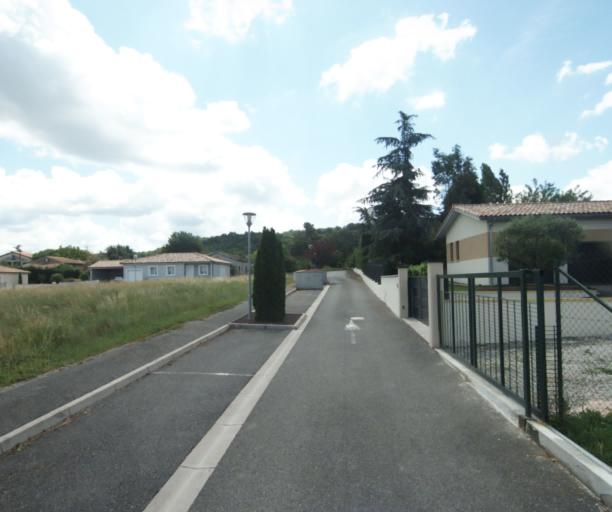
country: FR
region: Midi-Pyrenees
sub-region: Departement de la Haute-Garonne
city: Revel
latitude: 43.4491
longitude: 1.9949
